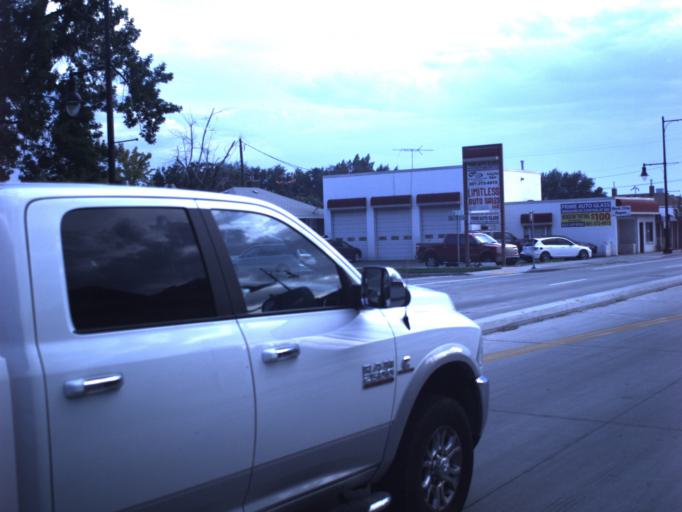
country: US
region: Utah
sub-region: Utah County
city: Provo
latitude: 40.2297
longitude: -111.6566
